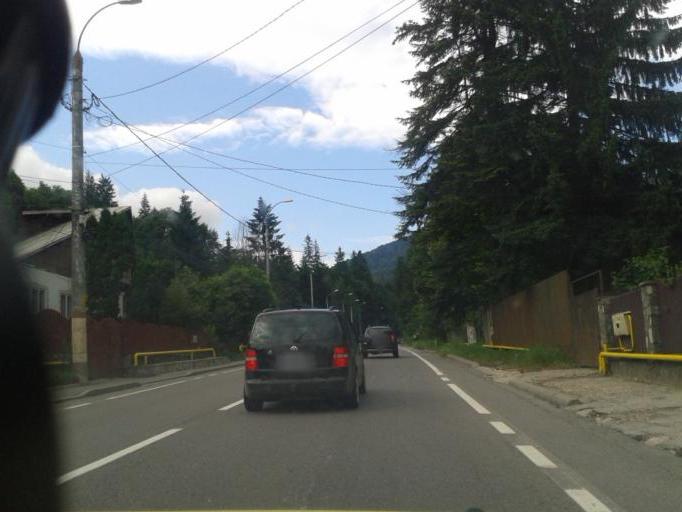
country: RO
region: Prahova
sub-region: Oras Sinaia
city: Sinaia
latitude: 45.3204
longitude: 25.5634
